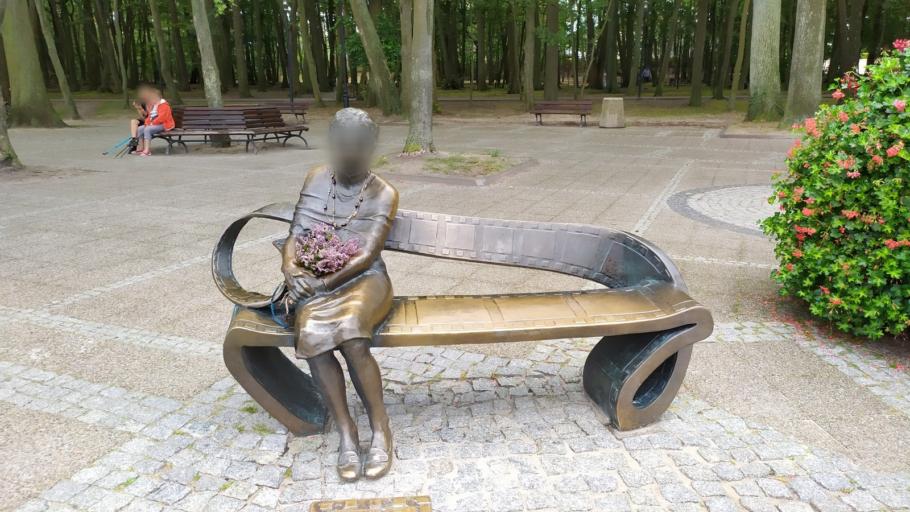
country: PL
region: Pomeranian Voivodeship
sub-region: Powiat slupski
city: Ustka
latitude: 54.5886
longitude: 16.8655
